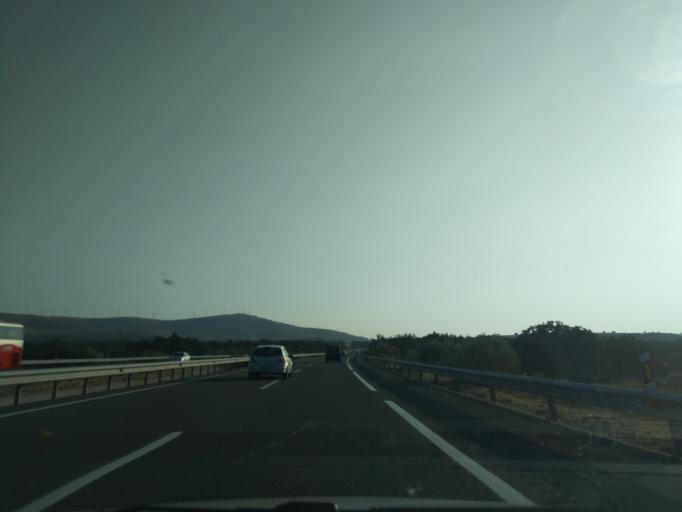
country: ES
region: Castille and Leon
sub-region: Provincia de Segovia
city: Villacastin
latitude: 40.7593
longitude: -4.4445
